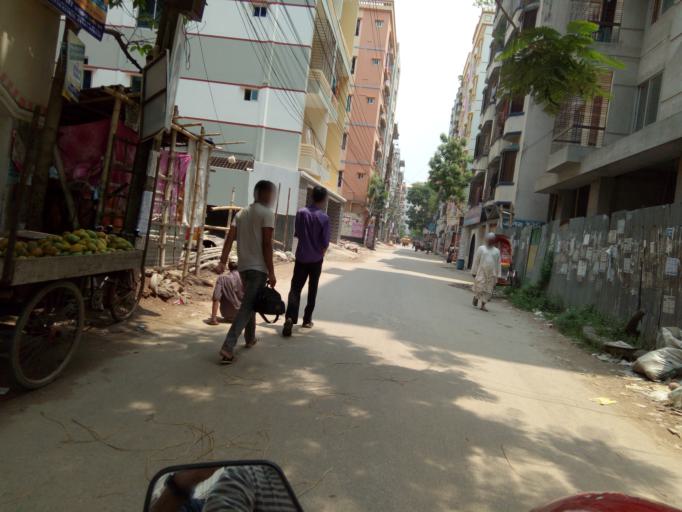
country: BD
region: Dhaka
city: Paltan
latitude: 23.7515
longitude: 90.4401
